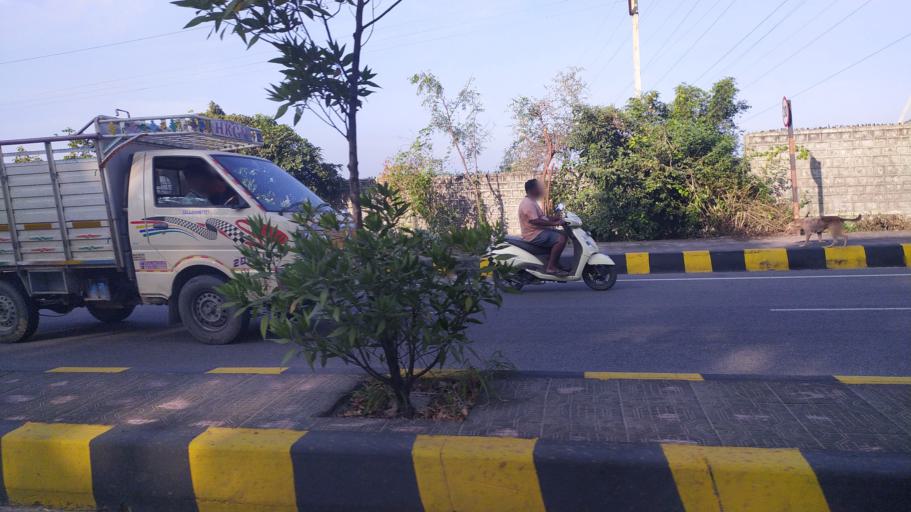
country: IN
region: Telangana
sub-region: Hyderabad
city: Hyderabad
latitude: 17.3288
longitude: 78.4092
